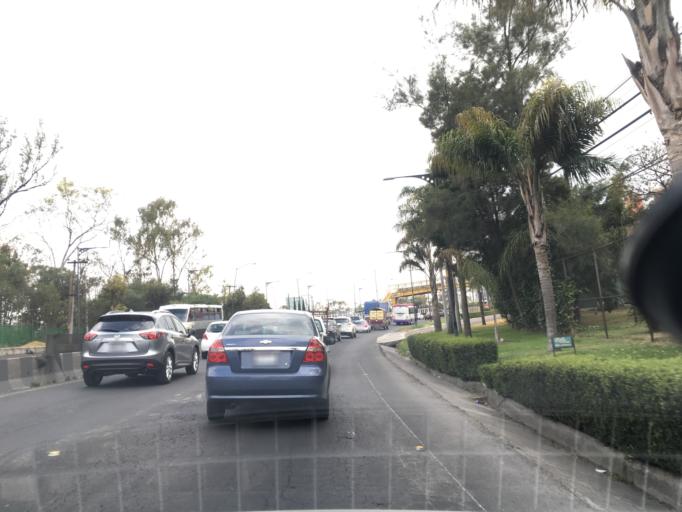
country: MX
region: Mexico City
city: Col. Bosques de las Lomas
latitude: 19.3707
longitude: -99.2696
